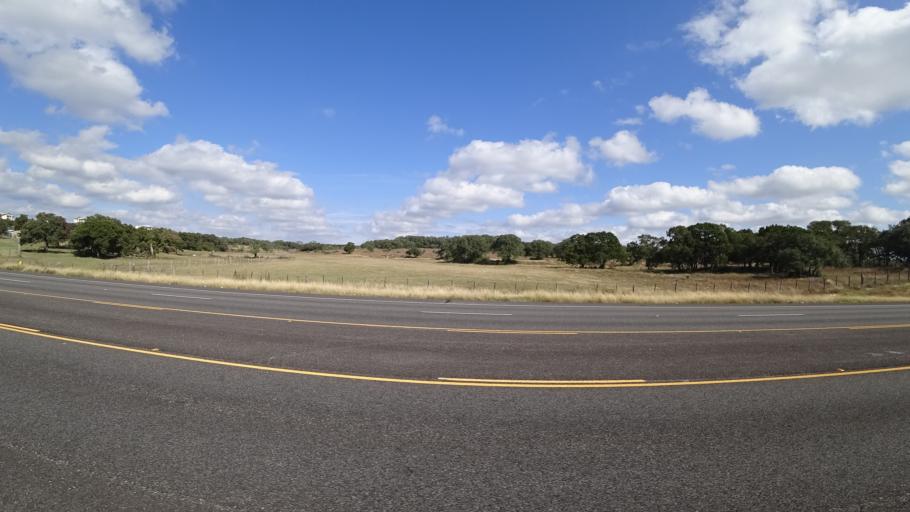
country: US
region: Texas
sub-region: Travis County
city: Barton Creek
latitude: 30.2539
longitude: -97.9012
